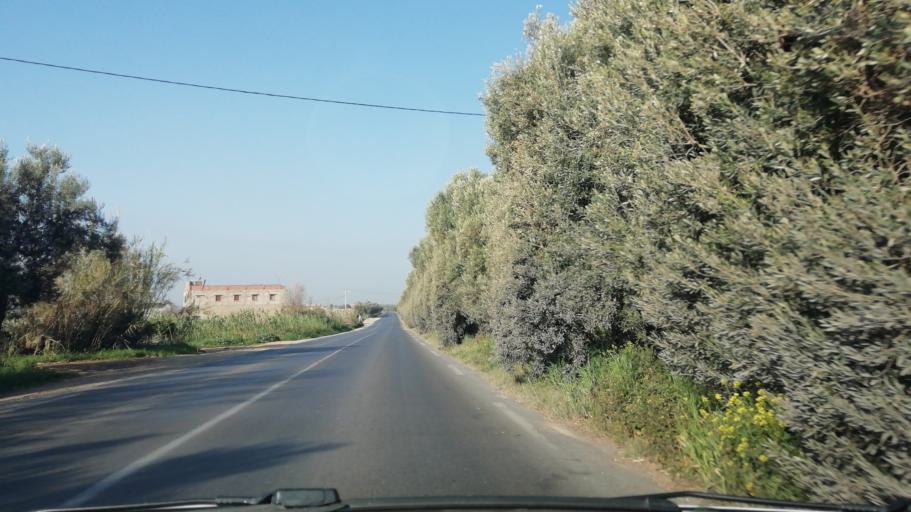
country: DZ
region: Mostaganem
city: Mostaganem
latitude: 35.7534
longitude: 0.1903
